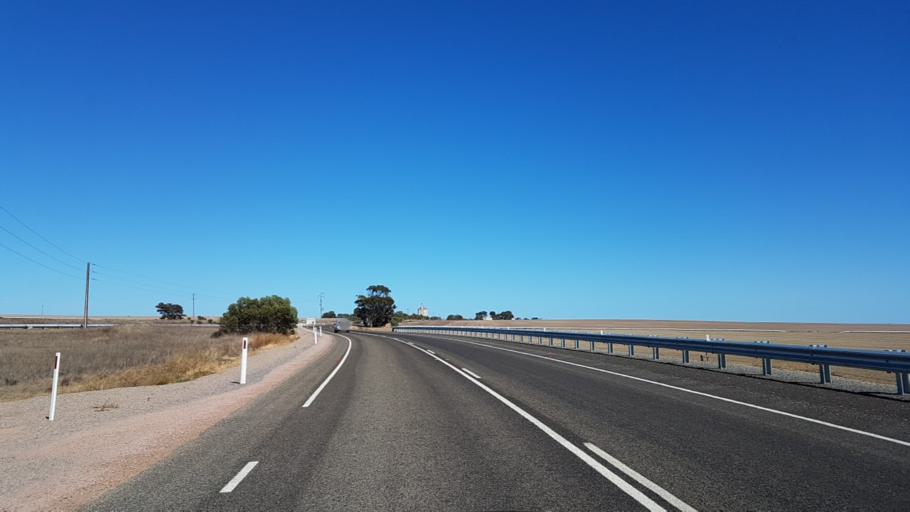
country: AU
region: South Australia
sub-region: Copper Coast
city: Kadina
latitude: -34.0413
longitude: 137.9222
